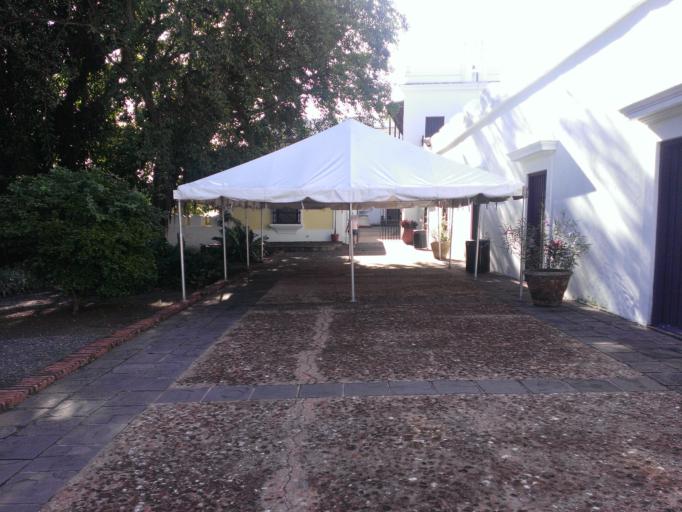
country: PR
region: San Juan
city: San Juan
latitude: 18.4667
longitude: -66.1201
